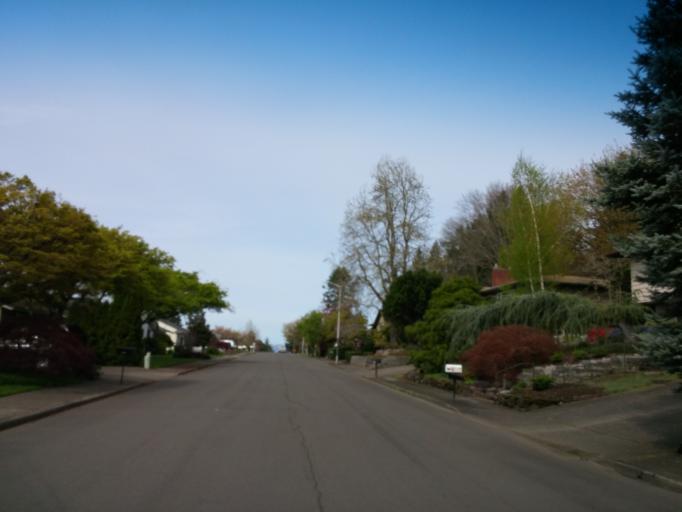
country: US
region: Oregon
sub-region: Washington County
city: Cedar Mill
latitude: 45.5311
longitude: -122.8003
